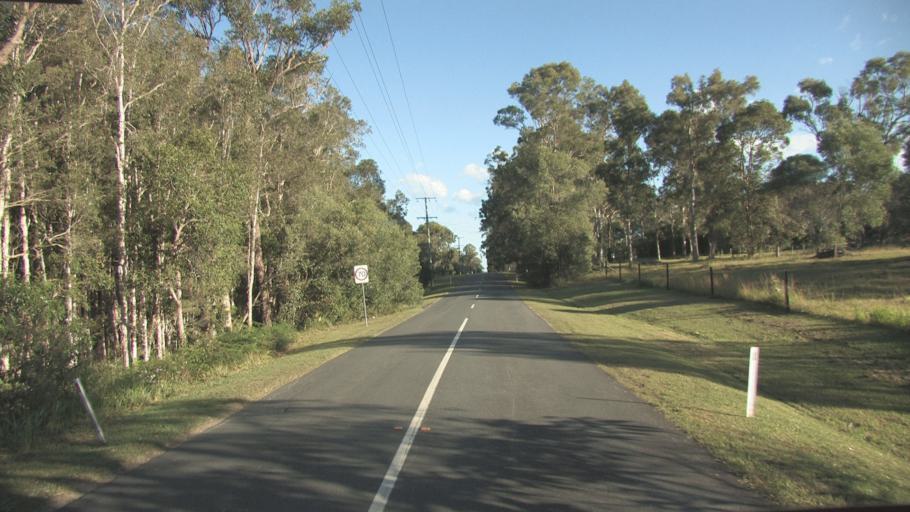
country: AU
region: Queensland
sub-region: Redland
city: Redland Bay
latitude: -27.6737
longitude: 153.2764
